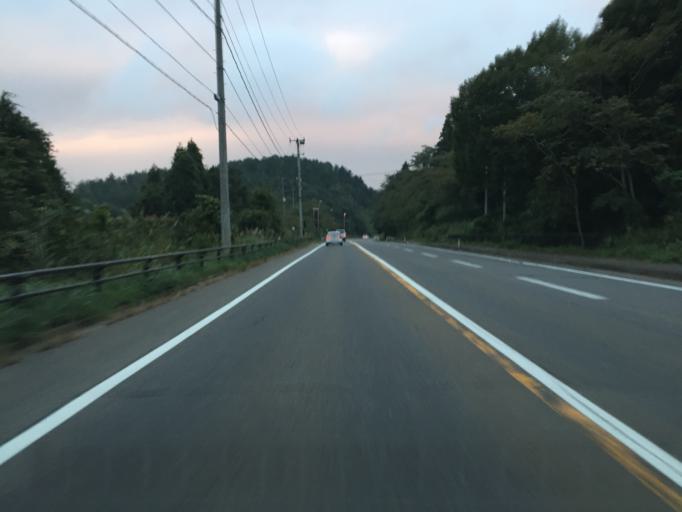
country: JP
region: Fukushima
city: Inawashiro
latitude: 37.5213
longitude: 139.9855
